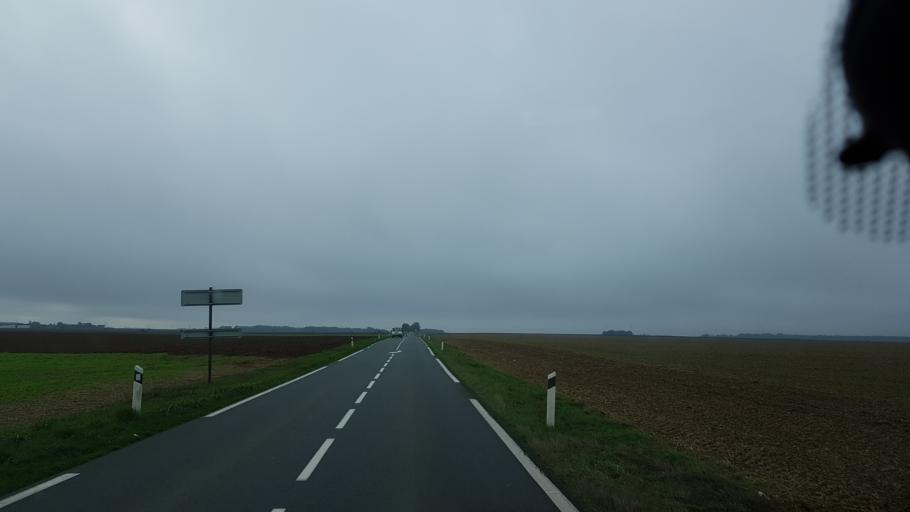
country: FR
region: Ile-de-France
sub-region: Departement de l'Essonne
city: Pussay
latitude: 48.4215
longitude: 1.9641
